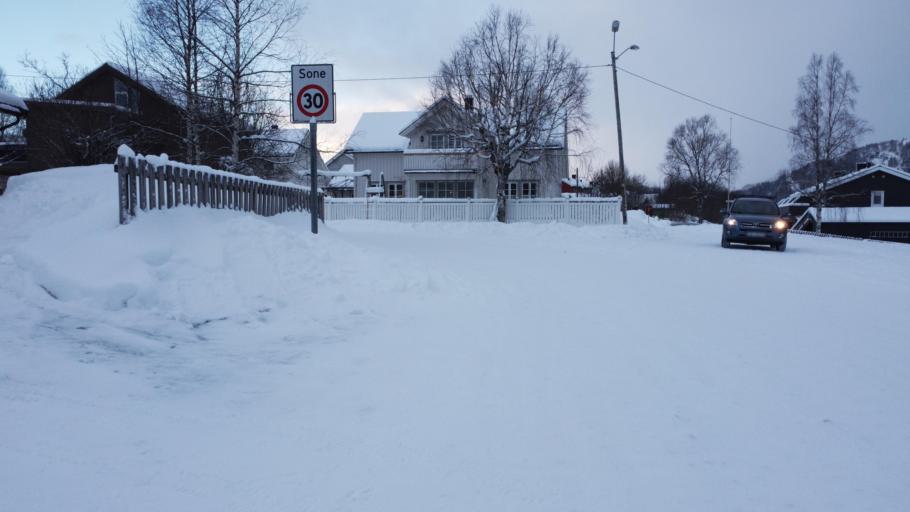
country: NO
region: Nordland
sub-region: Rana
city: Mo i Rana
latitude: 66.3188
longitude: 14.1664
